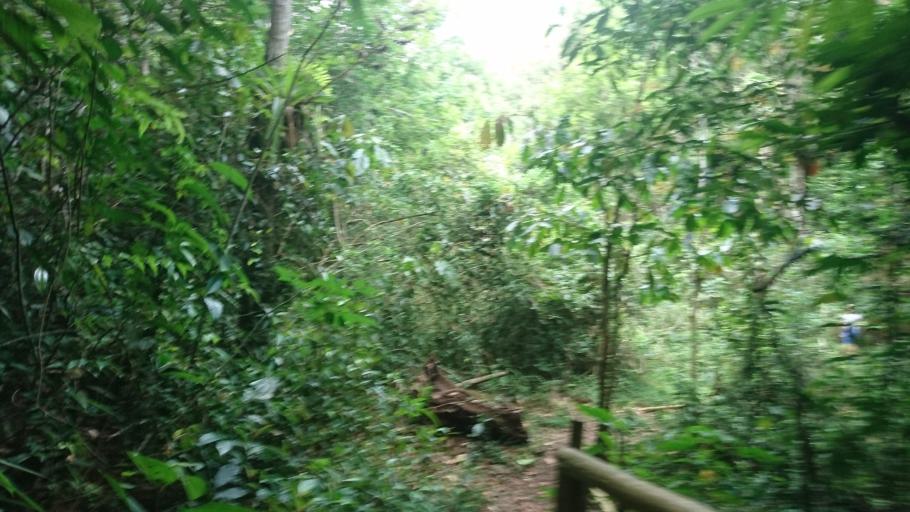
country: GT
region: Huehuetenango
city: Union
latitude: 16.1338
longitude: -91.7276
